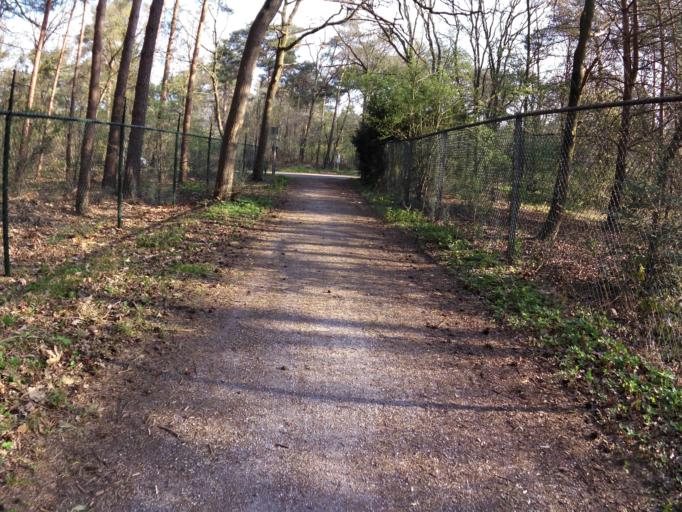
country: NL
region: North Brabant
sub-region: Gemeente Maasdonk
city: Geffen
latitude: 51.6958
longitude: 5.4188
